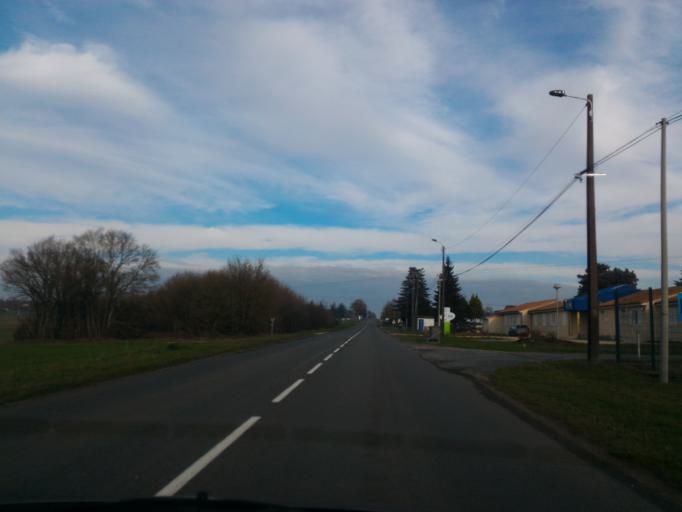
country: FR
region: Poitou-Charentes
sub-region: Departement de la Charente
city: Ruffec
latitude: 46.0412
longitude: 0.1976
